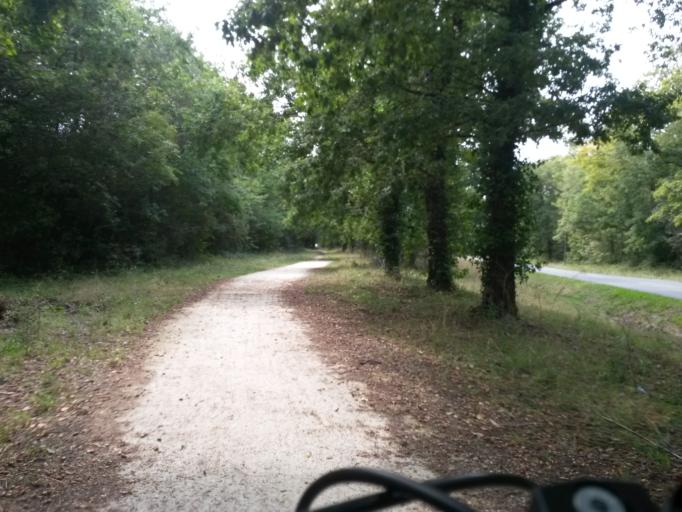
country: FR
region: Poitou-Charentes
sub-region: Departement de la Charente-Maritime
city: Dolus-d'Oleron
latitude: 45.8886
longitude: -1.2380
